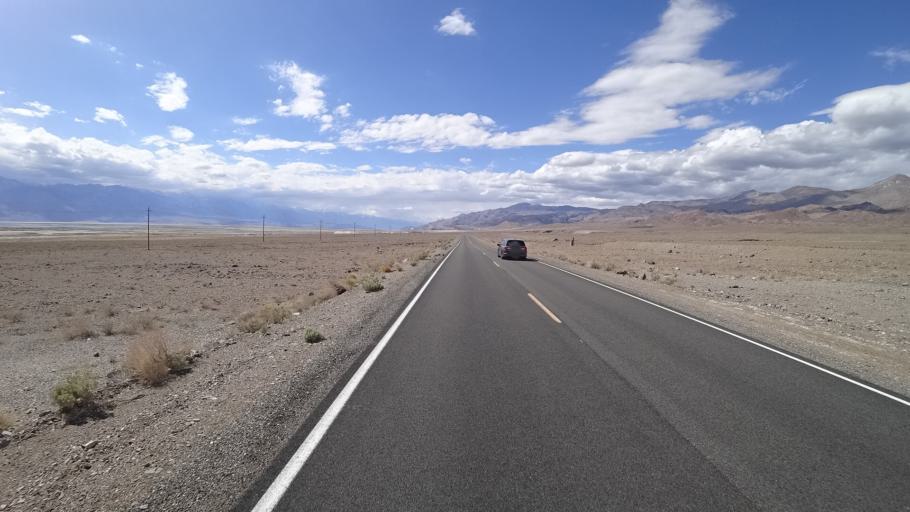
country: US
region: California
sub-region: Inyo County
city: Lone Pine
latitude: 36.4527
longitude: -117.8405
